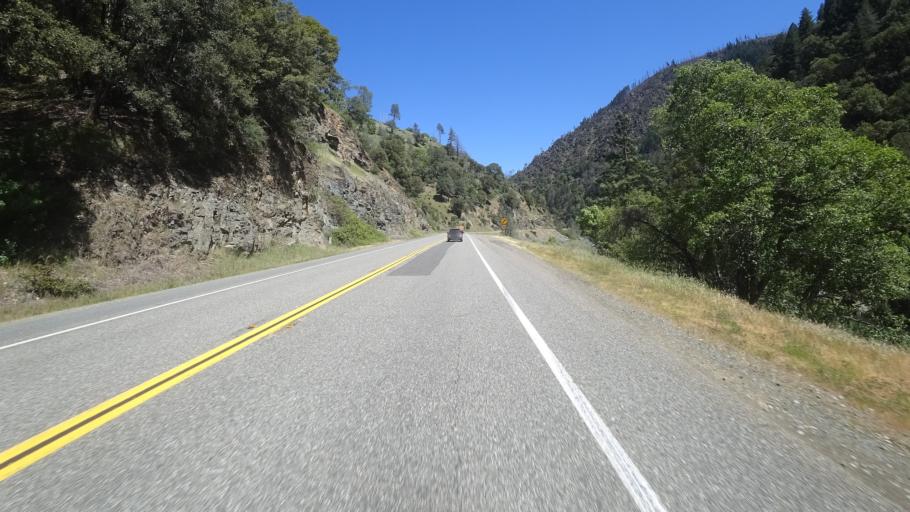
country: US
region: California
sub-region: Trinity County
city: Weaverville
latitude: 40.7639
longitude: -123.1445
